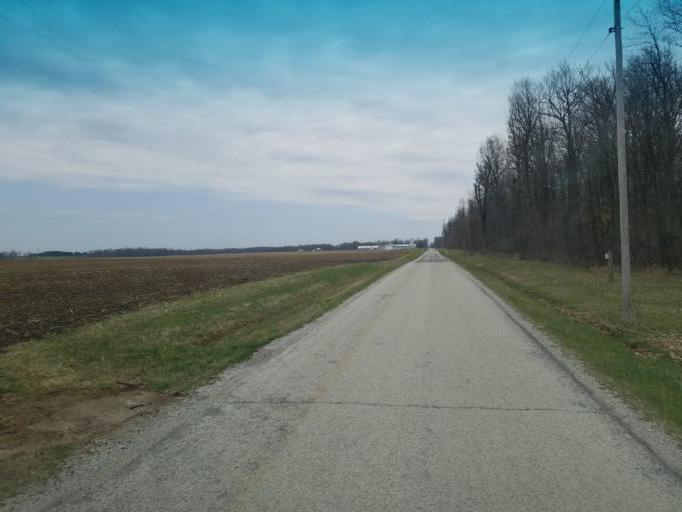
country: US
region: Ohio
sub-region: Crawford County
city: Bucyrus
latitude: 40.8920
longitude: -82.9851
